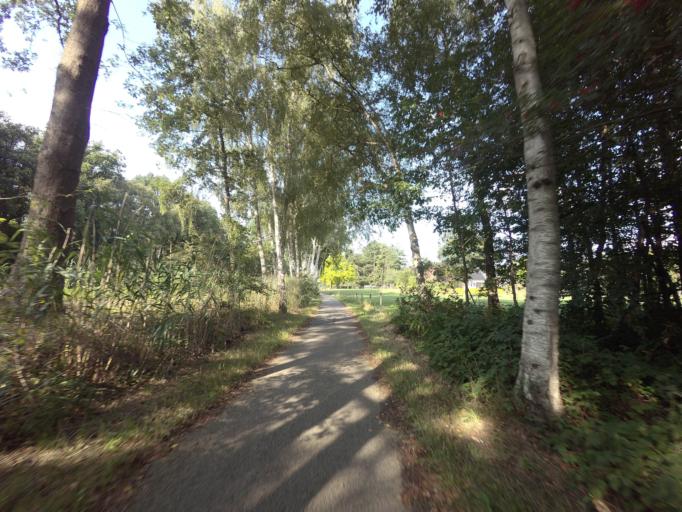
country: NL
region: Overijssel
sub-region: Gemeente Deventer
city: Schalkhaar
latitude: 52.2853
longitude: 6.2297
